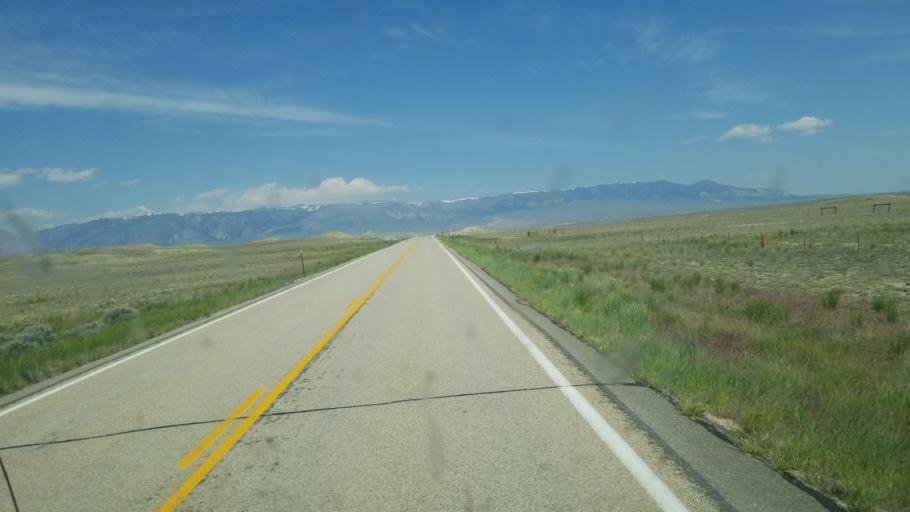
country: US
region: Wyoming
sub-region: Park County
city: Powell
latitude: 44.8703
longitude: -109.0458
